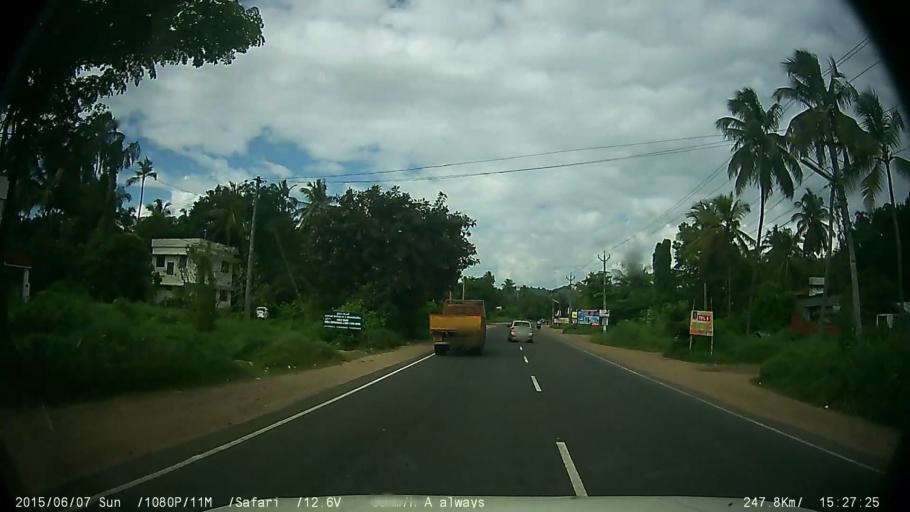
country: IN
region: Kerala
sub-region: Thrissur District
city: Trichur
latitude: 10.5372
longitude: 76.2713
